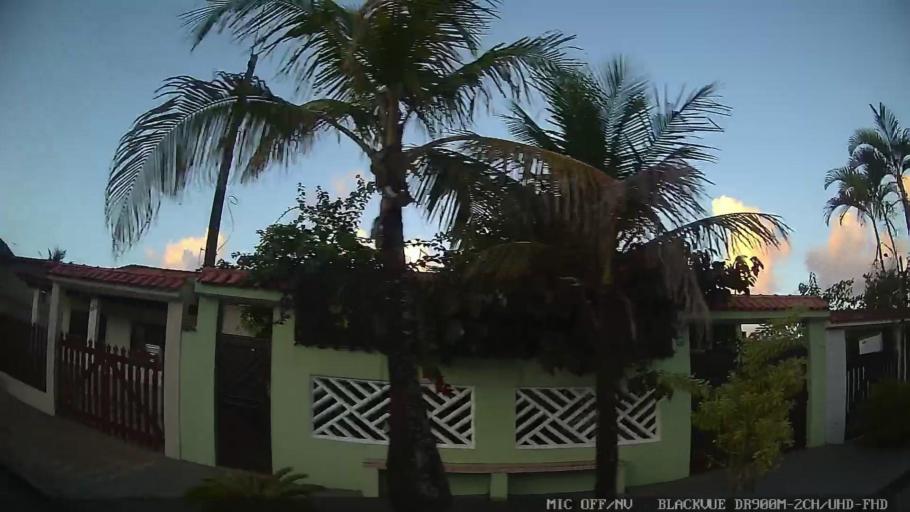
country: BR
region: Sao Paulo
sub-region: Itanhaem
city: Itanhaem
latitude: -24.1473
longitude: -46.7316
